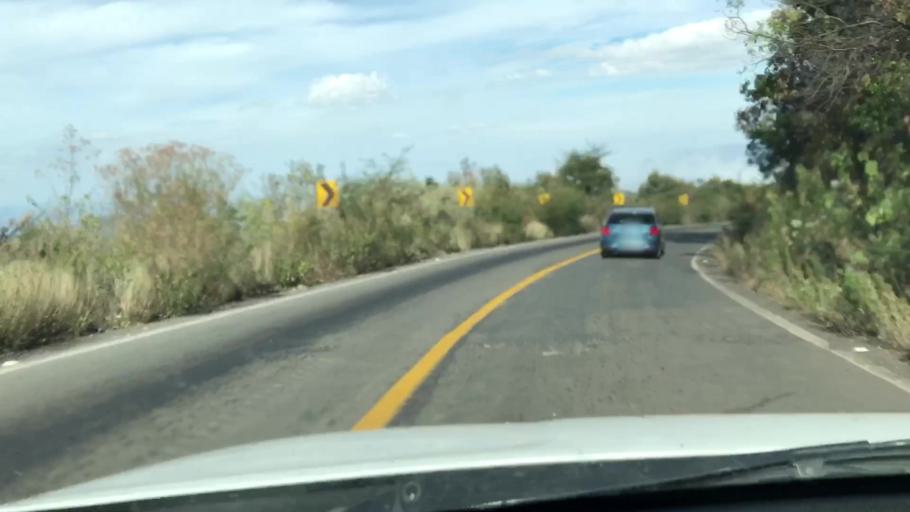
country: MX
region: Jalisco
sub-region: Zacoalco de Torres
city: Barranca de Otates (Barranca de Otatan)
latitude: 20.2015
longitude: -103.6961
